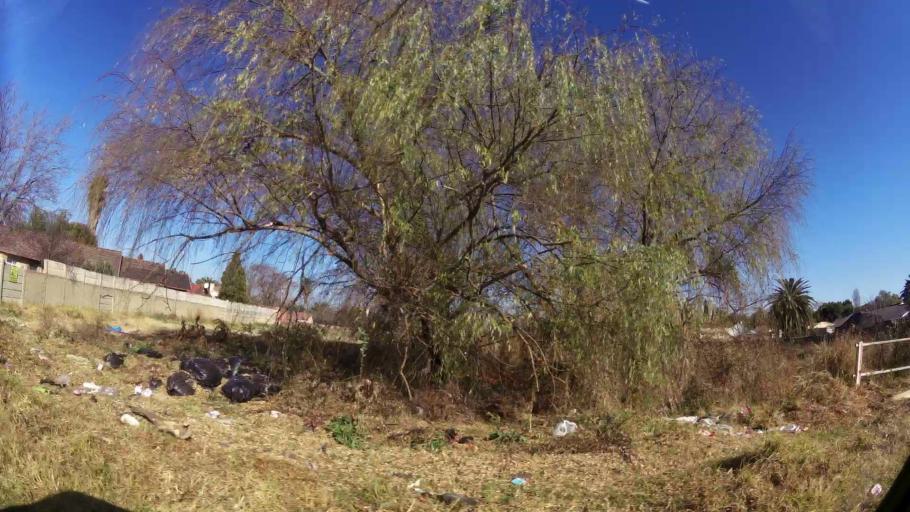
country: ZA
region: Gauteng
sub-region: Ekurhuleni Metropolitan Municipality
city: Germiston
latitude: -26.3415
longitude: 28.0994
